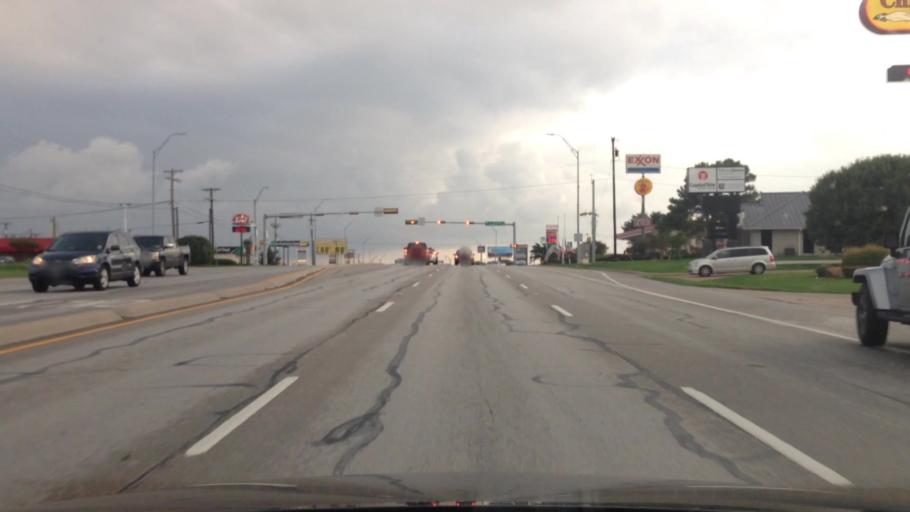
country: US
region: Texas
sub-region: Johnson County
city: Burleson
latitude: 32.5443
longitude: -97.3291
